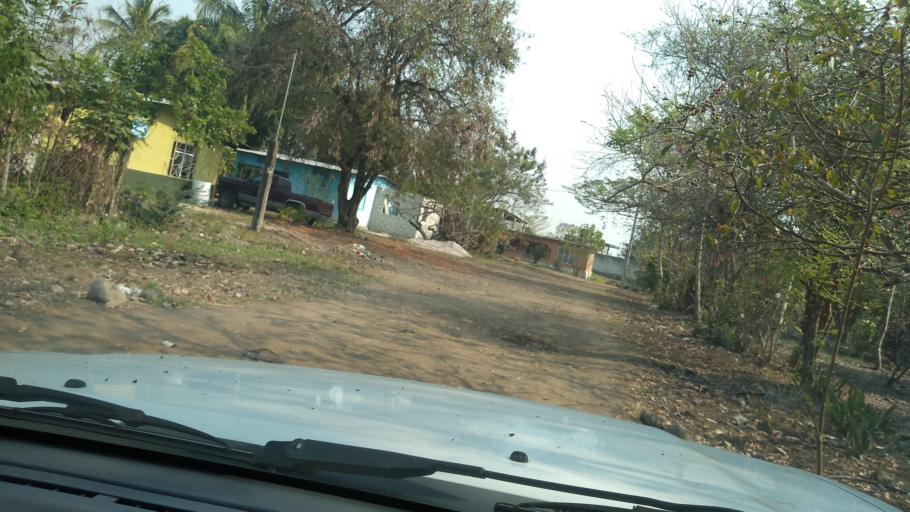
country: MX
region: Oaxaca
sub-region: Cosolapa
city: Cosolapa
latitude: 18.6244
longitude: -96.6039
